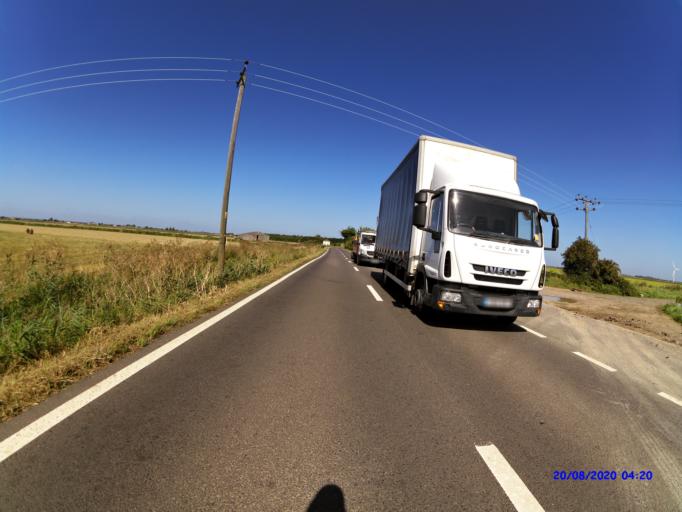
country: GB
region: England
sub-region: Cambridgeshire
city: Ramsey
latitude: 52.4942
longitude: -0.1210
